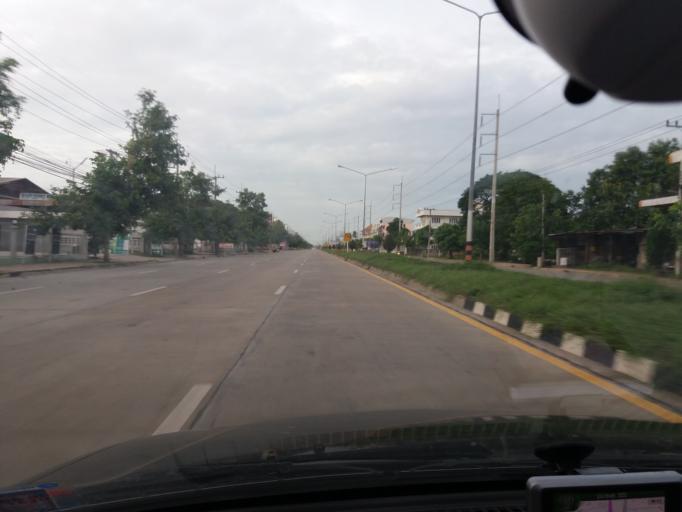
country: TH
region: Suphan Buri
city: U Thong
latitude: 14.3930
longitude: 99.8955
